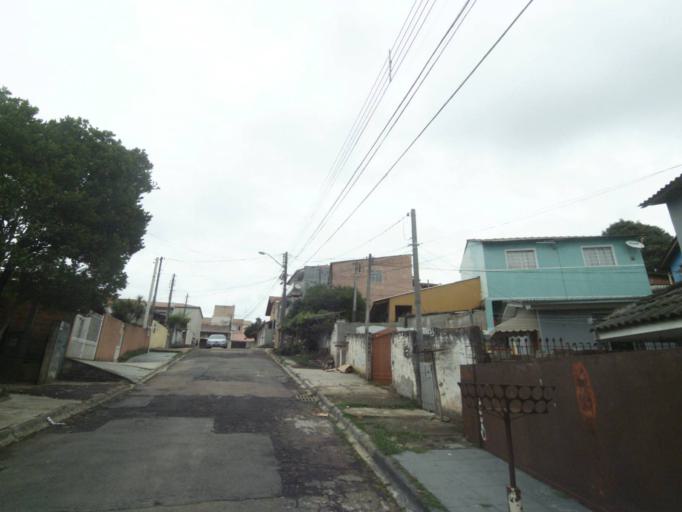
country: BR
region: Parana
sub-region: Curitiba
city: Curitiba
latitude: -25.4574
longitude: -49.3246
